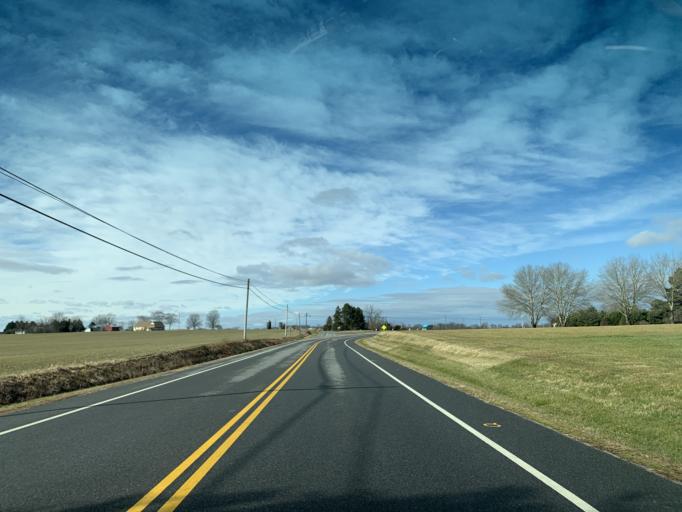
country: US
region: Maryland
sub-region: Kent County
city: Chestertown
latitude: 39.3304
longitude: -76.0581
